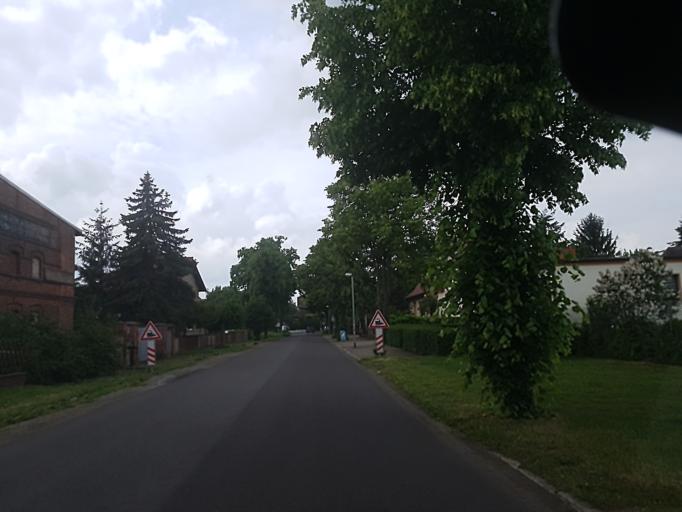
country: DE
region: Saxony-Anhalt
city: Loburg
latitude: 52.1175
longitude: 12.0887
